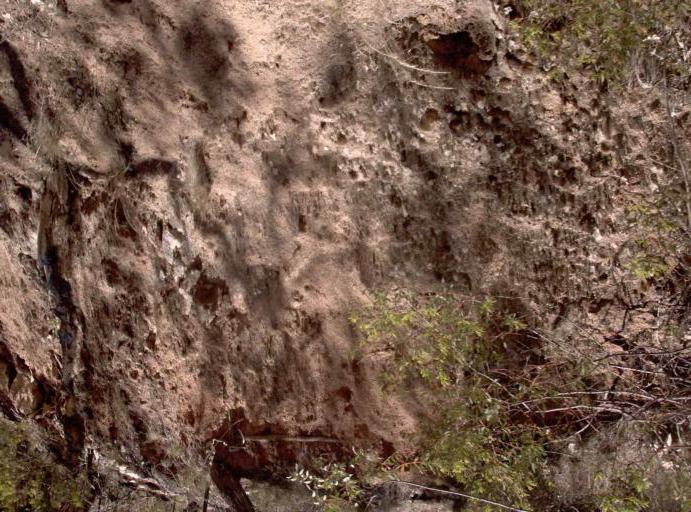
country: AU
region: New South Wales
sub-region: Snowy River
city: Jindabyne
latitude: -36.9141
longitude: 148.4214
